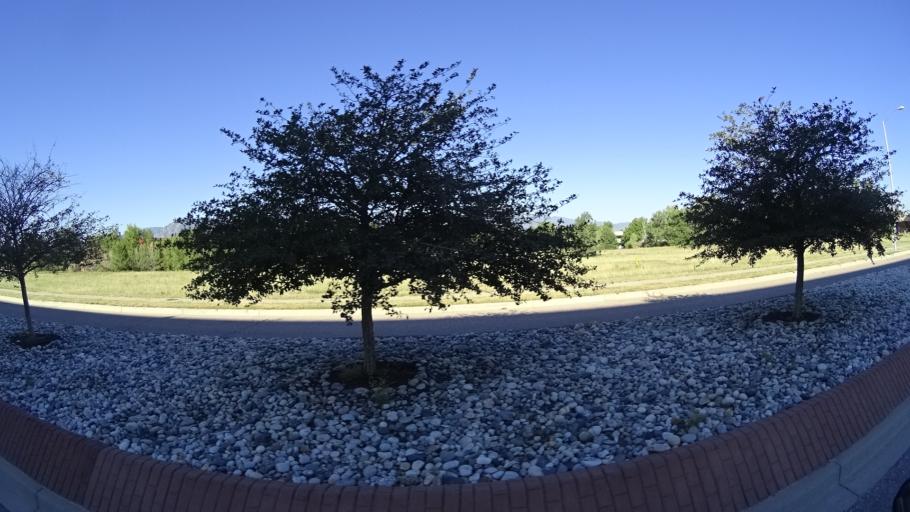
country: US
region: Colorado
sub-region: El Paso County
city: Cimarron Hills
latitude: 38.8076
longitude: -104.7237
